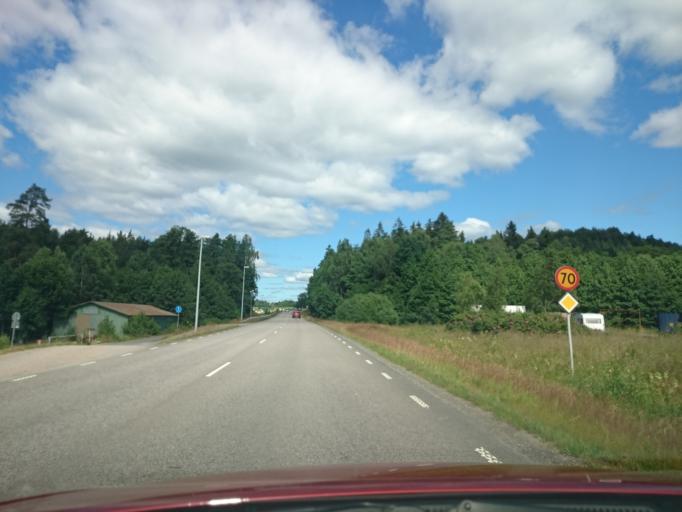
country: SE
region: Vaestra Goetaland
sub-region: Lerums Kommun
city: Stenkullen
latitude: 57.8053
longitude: 12.3050
